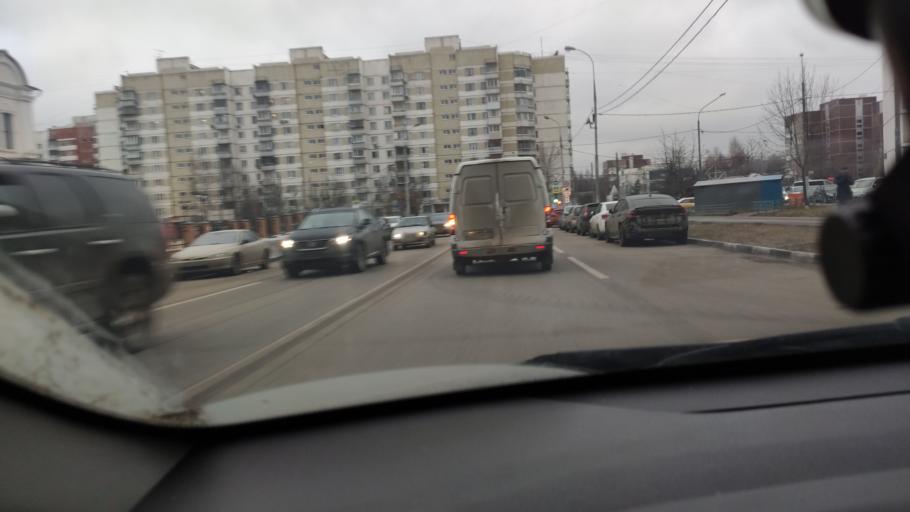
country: RU
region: Moskovskaya
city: Shcherbinka
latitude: 55.5447
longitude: 37.5412
